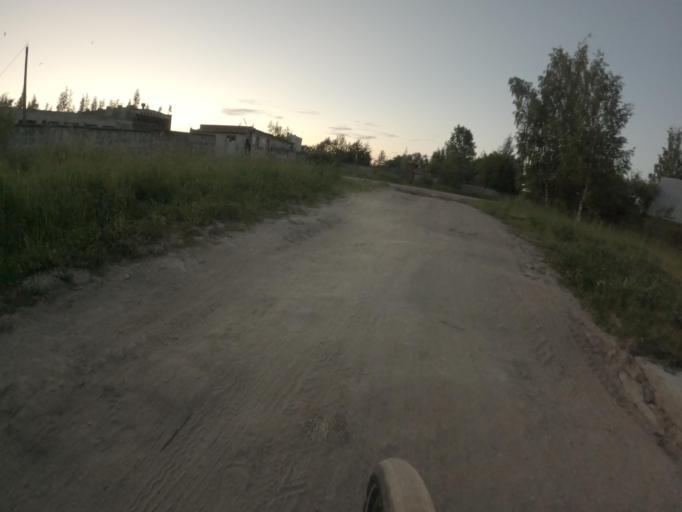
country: RU
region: St.-Petersburg
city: Sapernyy
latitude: 59.7823
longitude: 30.6741
